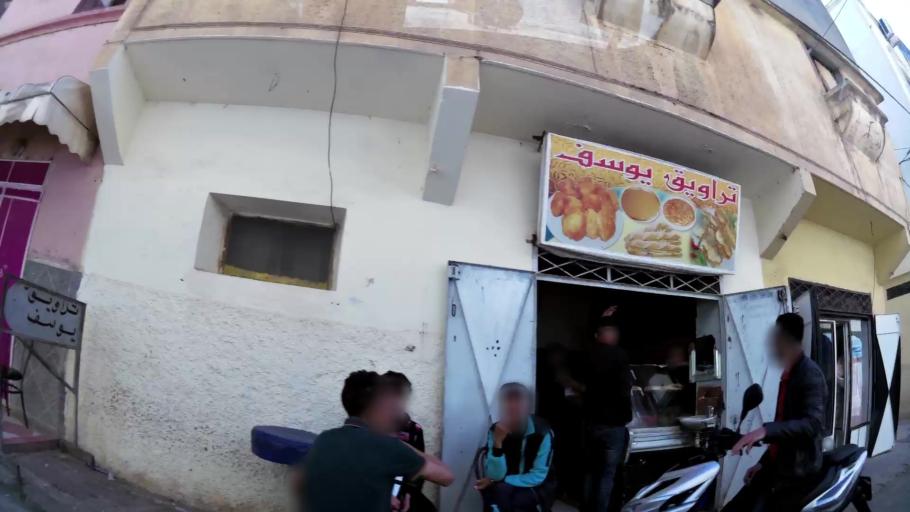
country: MA
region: Meknes-Tafilalet
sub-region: Meknes
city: Meknes
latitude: 33.8831
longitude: -5.5748
